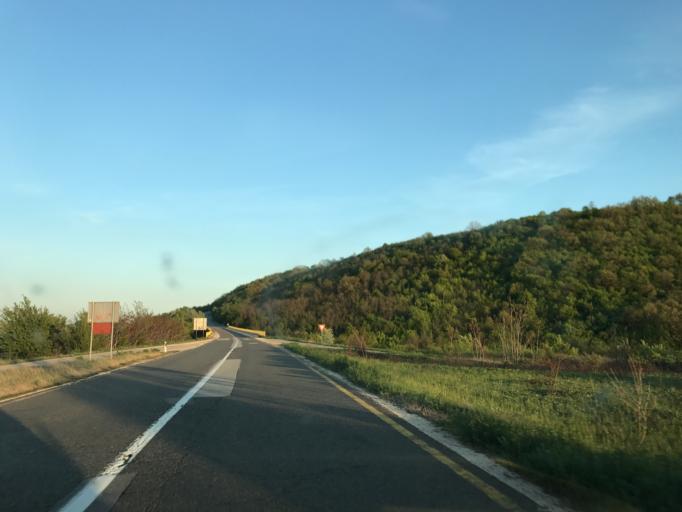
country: RO
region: Mehedinti
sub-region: Comuna Gogosu
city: Ostrovu Mare
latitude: 44.4290
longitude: 22.4676
